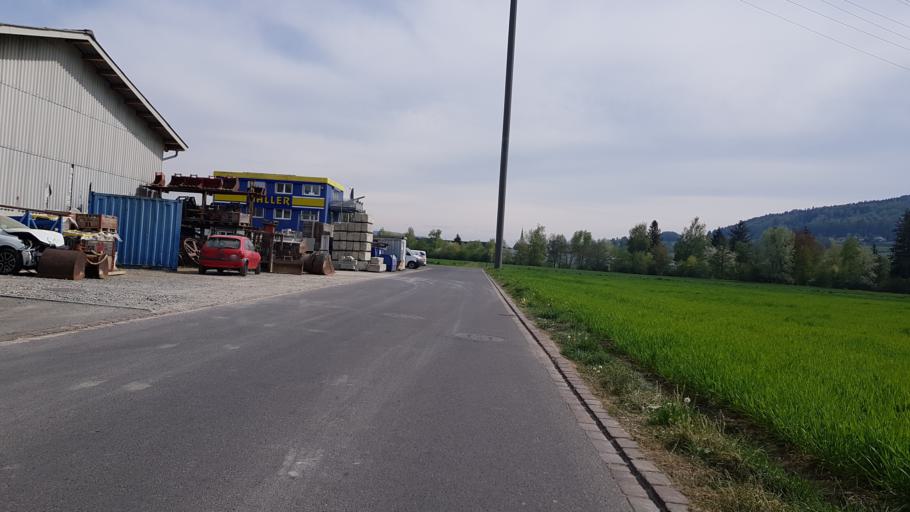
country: CH
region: Aargau
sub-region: Bezirk Kulm
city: Reinach
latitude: 47.2620
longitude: 8.1727
